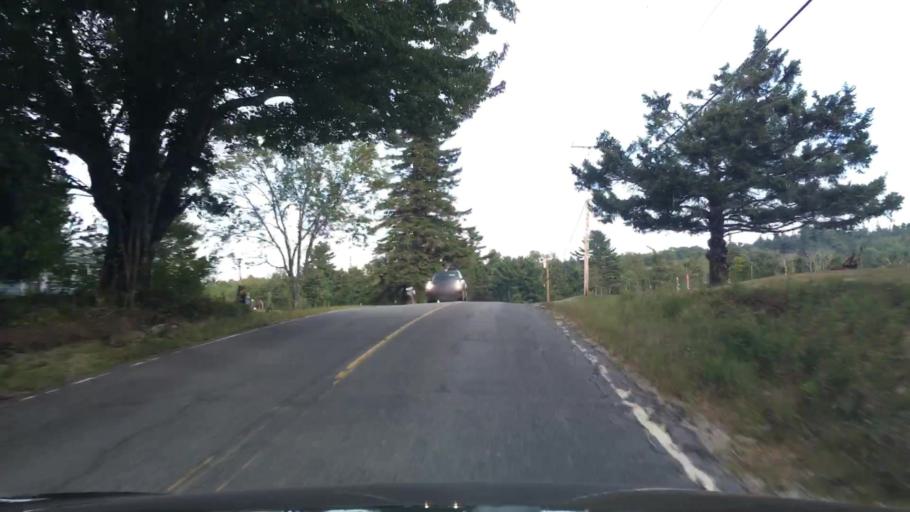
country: US
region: Maine
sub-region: Hancock County
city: Surry
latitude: 44.4942
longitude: -68.5192
